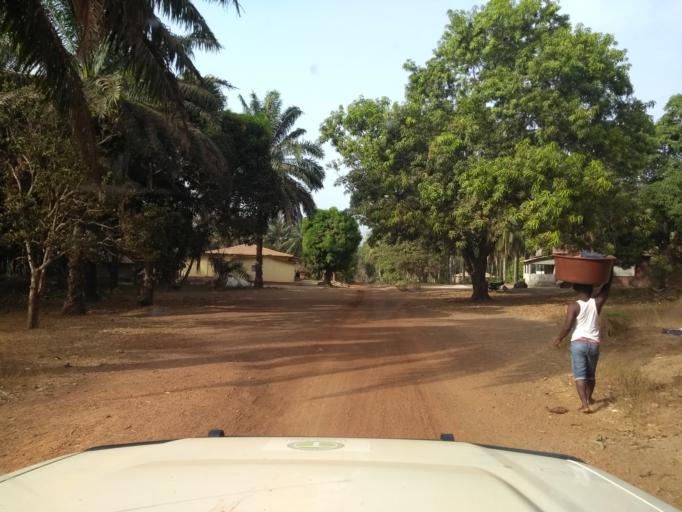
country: GN
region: Kindia
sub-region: Prefecture de Dubreka
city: Dubreka
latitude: 9.8598
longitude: -13.5471
